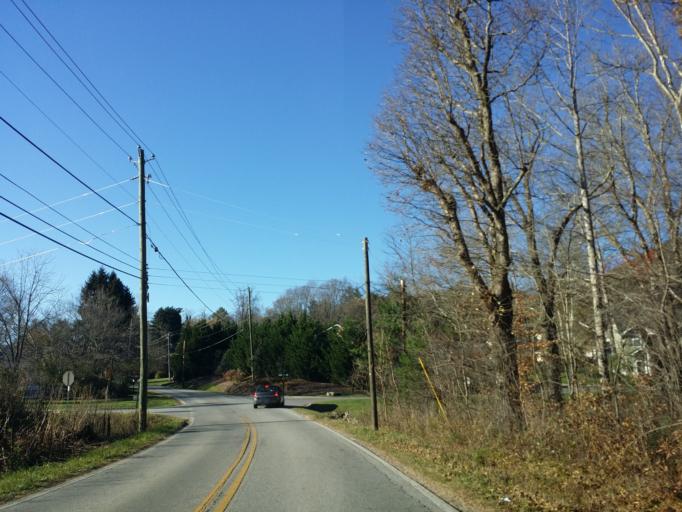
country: US
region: North Carolina
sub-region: Buncombe County
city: Swannanoa
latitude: 35.6059
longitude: -82.4096
